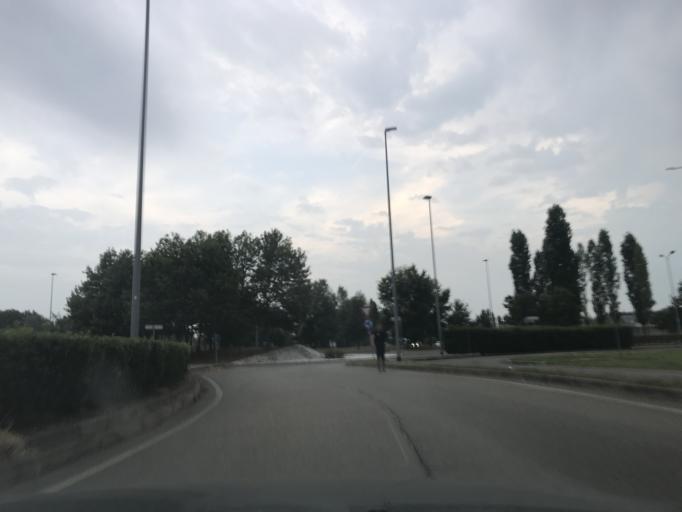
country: IT
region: Lombardy
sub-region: Citta metropolitana di Milano
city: Rozzano
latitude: 45.4051
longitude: 9.1555
